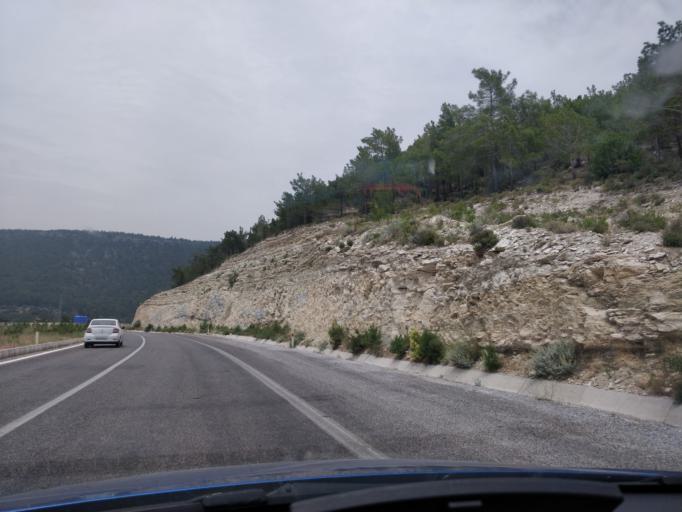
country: TR
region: Mersin
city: Tasucu
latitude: 36.3965
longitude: 33.8452
